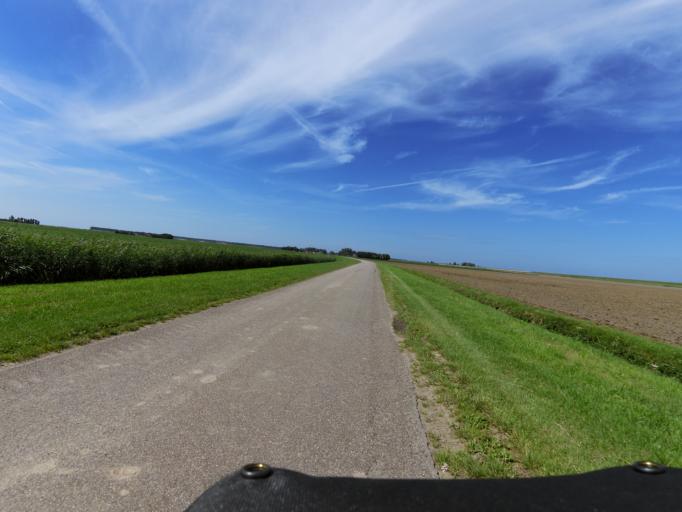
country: NL
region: South Holland
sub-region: Gemeente Goeree-Overflakkee
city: Dirksland
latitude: 51.7954
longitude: 4.1049
